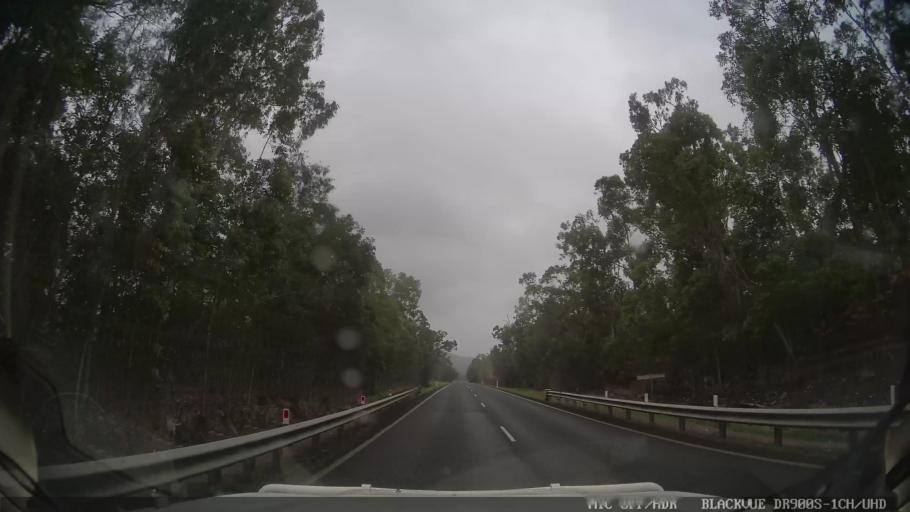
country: AU
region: Queensland
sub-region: Hinchinbrook
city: Ingham
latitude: -18.4446
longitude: 146.1407
